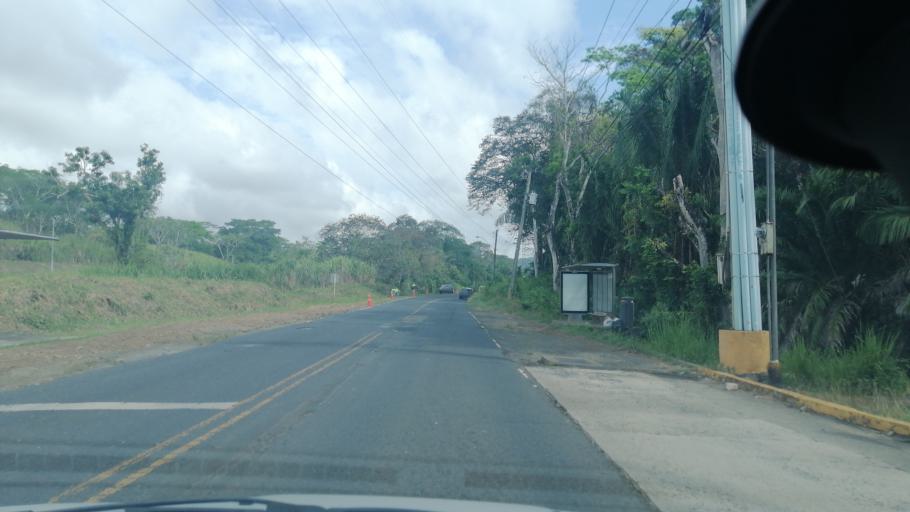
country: PA
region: Panama
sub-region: Distrito de Panama
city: Paraiso
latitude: 9.0469
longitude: -79.6365
